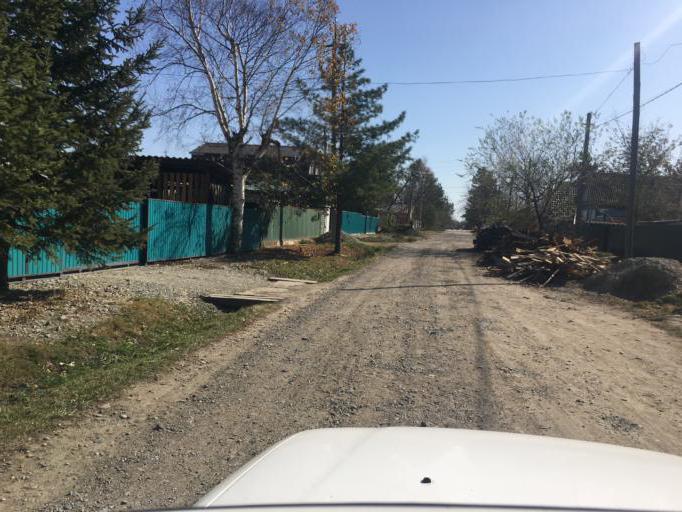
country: RU
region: Primorskiy
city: Dal'nerechensk
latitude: 45.9304
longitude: 133.7475
